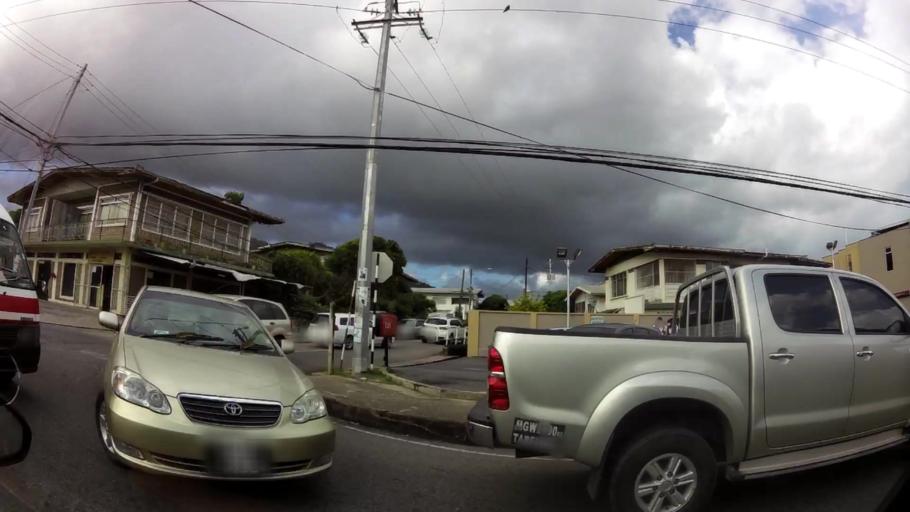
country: TT
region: Tunapuna/Piarco
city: Paradise
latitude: 10.6460
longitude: -61.3735
